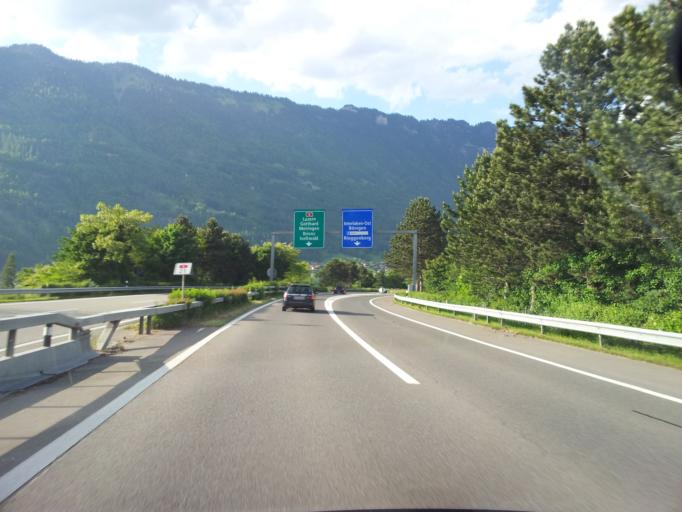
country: CH
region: Bern
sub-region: Interlaken-Oberhasli District
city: Matten
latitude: 46.6810
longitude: 7.8757
